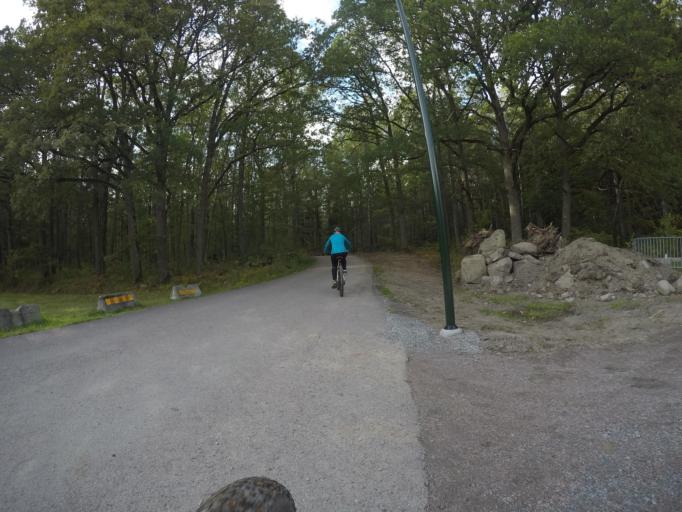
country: SE
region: Vaestmanland
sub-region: Kopings Kommun
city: Koping
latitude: 59.5089
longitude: 16.0201
